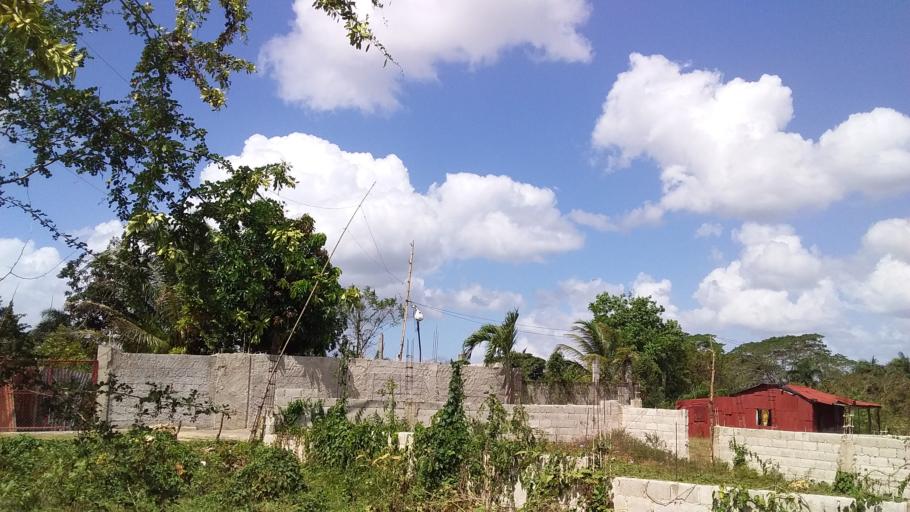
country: DO
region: Santo Domingo
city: Guerra
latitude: 18.5642
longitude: -69.7814
